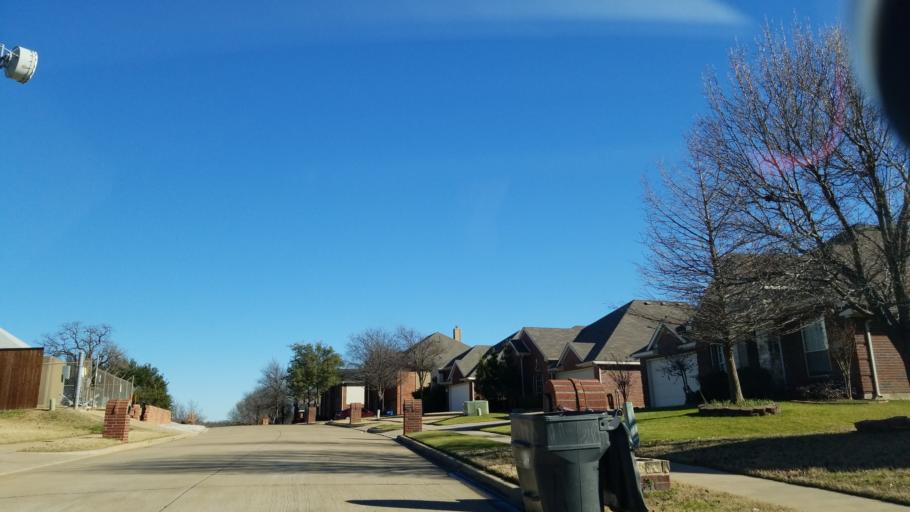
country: US
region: Texas
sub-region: Denton County
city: Corinth
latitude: 33.1444
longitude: -97.0844
